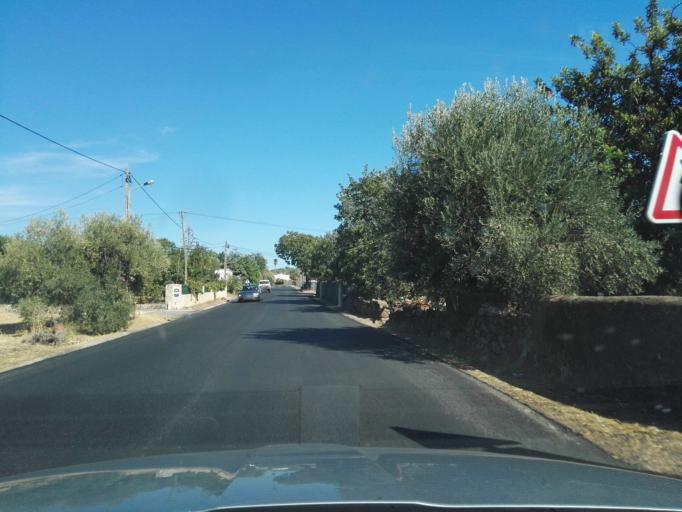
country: PT
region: Faro
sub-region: Olhao
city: Moncarapacho
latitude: 37.1530
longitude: -7.7811
